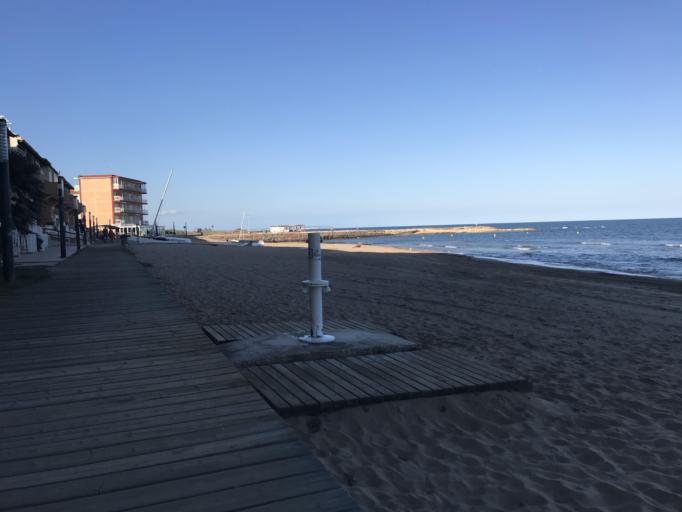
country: ES
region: Valencia
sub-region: Provincia de Alicante
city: Torrevieja
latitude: 38.0277
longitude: -0.6525
